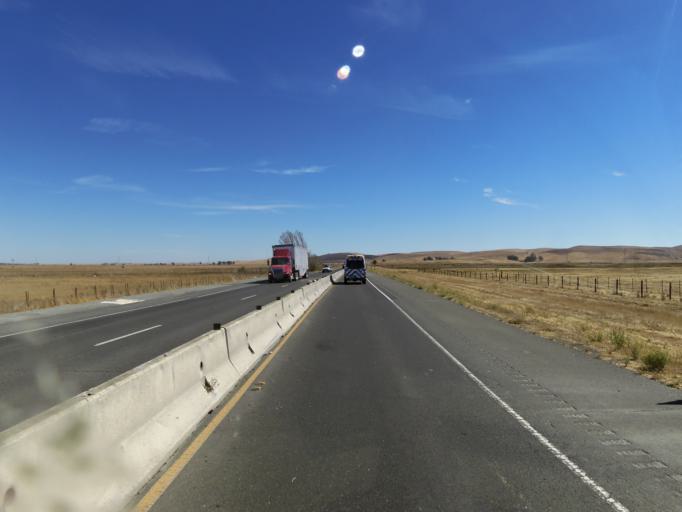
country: US
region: California
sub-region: Solano County
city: Suisun
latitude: 38.2371
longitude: -121.9859
